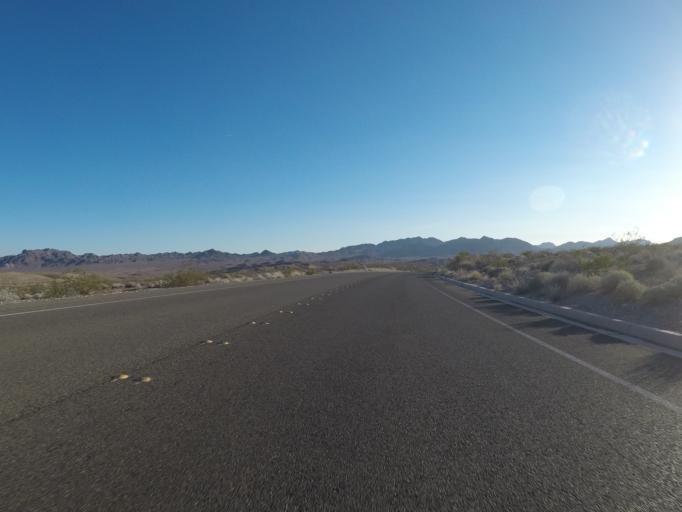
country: US
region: Nevada
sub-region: Clark County
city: Moapa Valley
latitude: 36.3170
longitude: -114.4918
